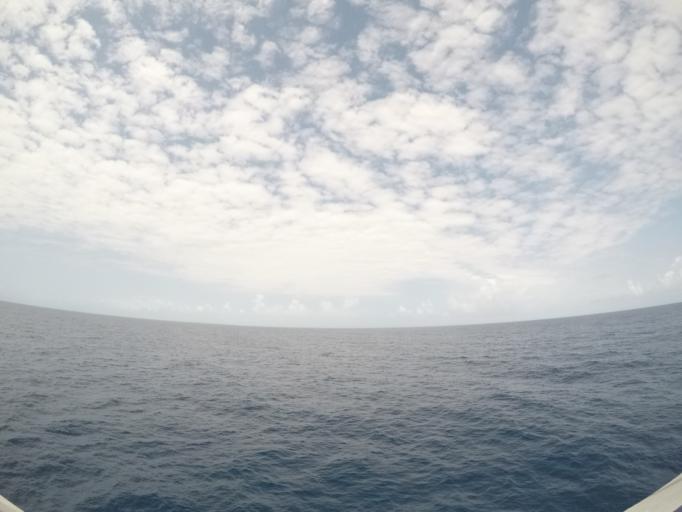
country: TZ
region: Zanzibar North
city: Nungwi
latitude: -5.5885
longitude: 39.3514
